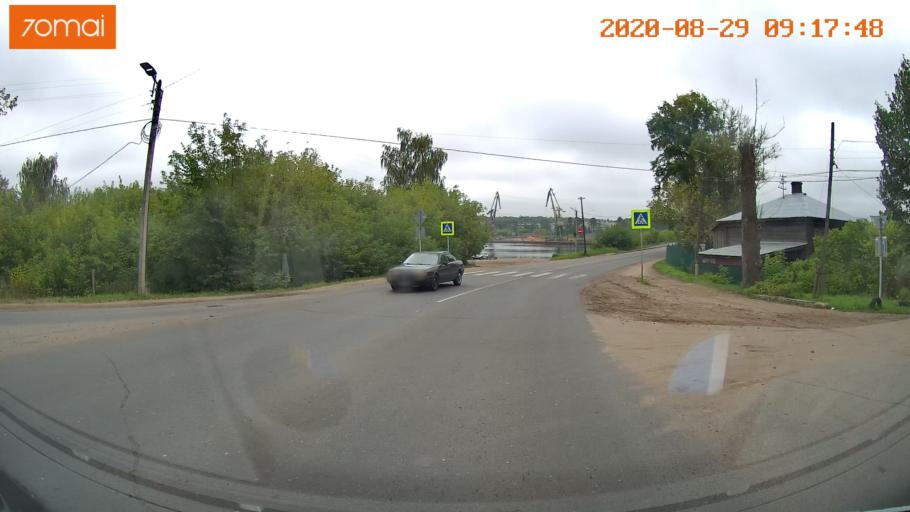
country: RU
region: Ivanovo
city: Kineshma
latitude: 57.4423
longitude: 42.1537
